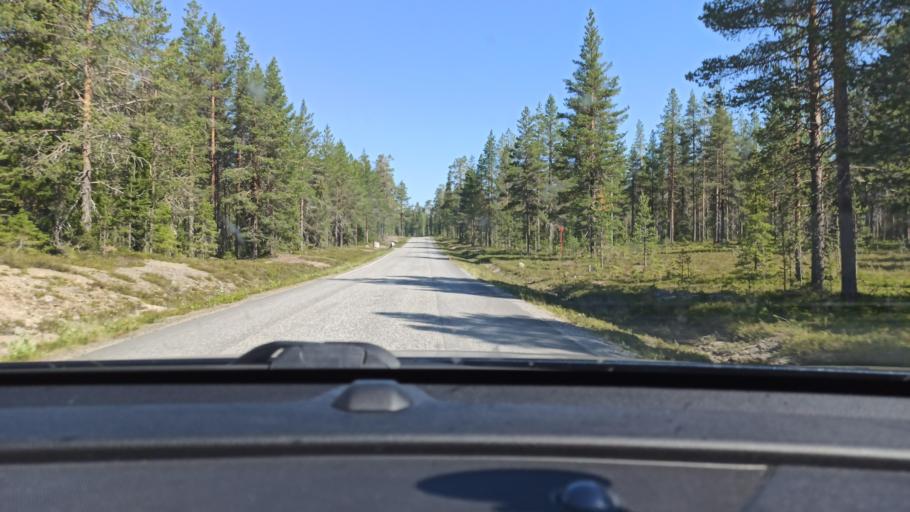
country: FI
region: Lapland
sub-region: Tunturi-Lappi
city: Kolari
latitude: 67.6571
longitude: 24.1648
